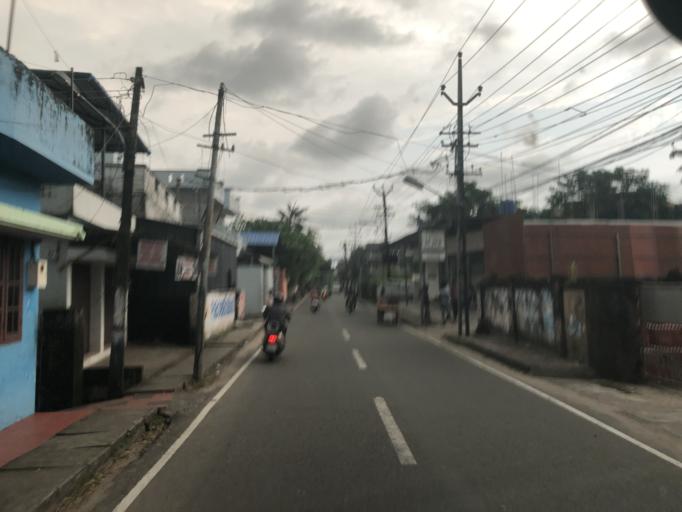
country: IN
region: Kerala
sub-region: Ernakulam
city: Cochin
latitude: 9.9546
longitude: 76.2578
